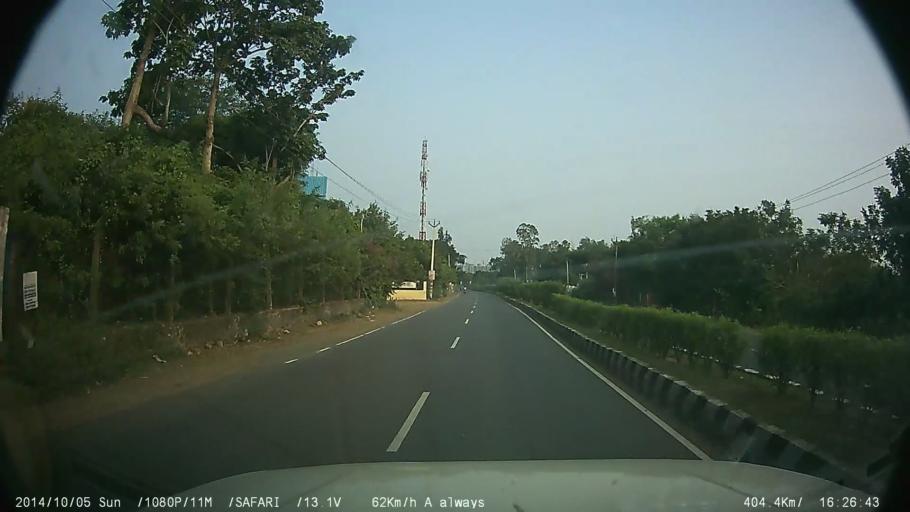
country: IN
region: Tamil Nadu
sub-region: Kancheepuram
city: Vengavasal
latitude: 12.8053
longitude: 80.1902
